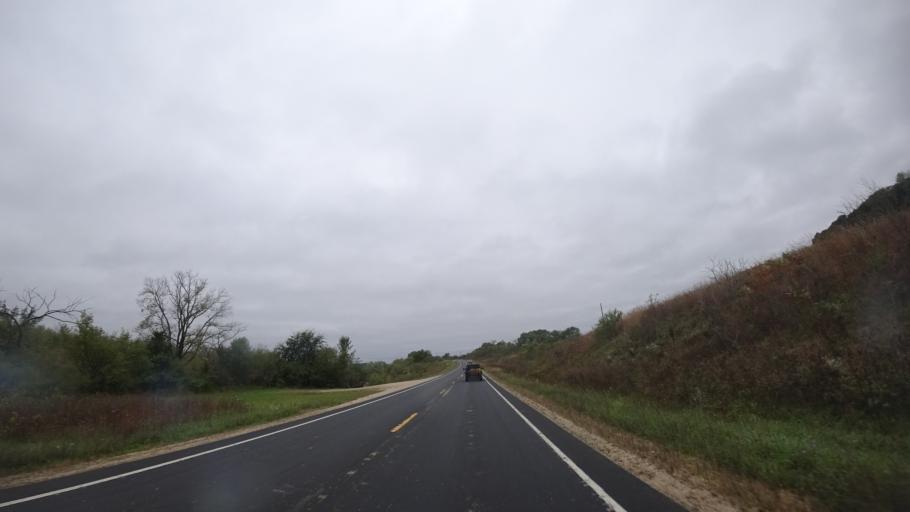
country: US
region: Wisconsin
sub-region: Grant County
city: Boscobel
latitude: 43.1163
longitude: -90.7896
